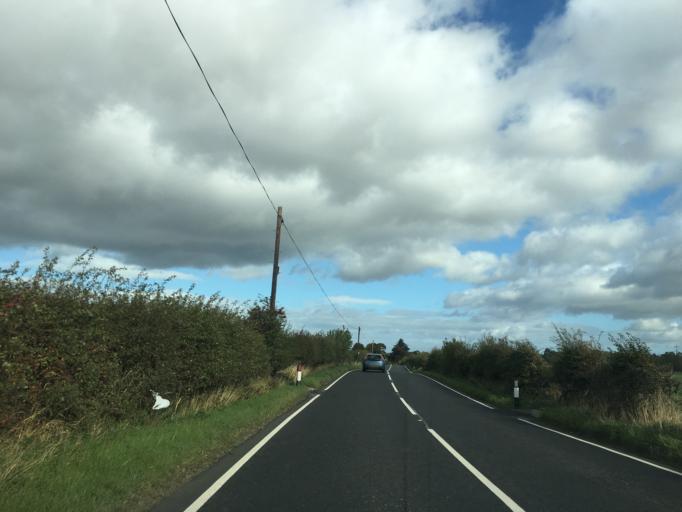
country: GB
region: Scotland
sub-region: Fife
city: Pathhead
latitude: 55.8898
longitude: -2.9753
